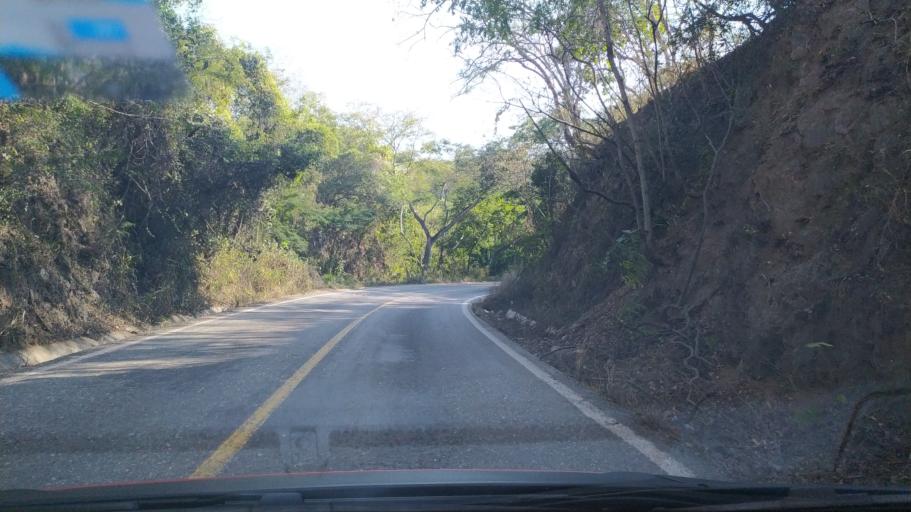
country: MX
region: Michoacan
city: Coahuayana Viejo
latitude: 18.6098
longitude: -103.6782
